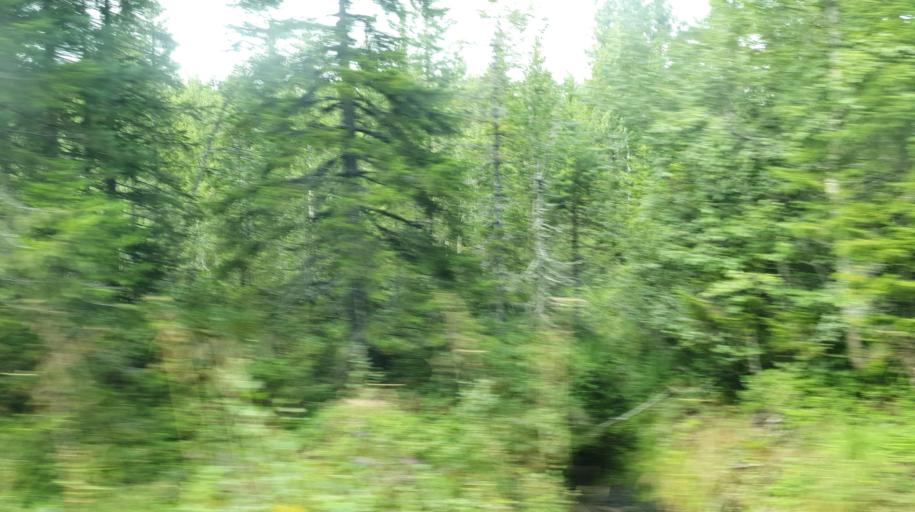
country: NO
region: Nord-Trondelag
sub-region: Levanger
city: Skogn
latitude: 63.5583
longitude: 11.1681
